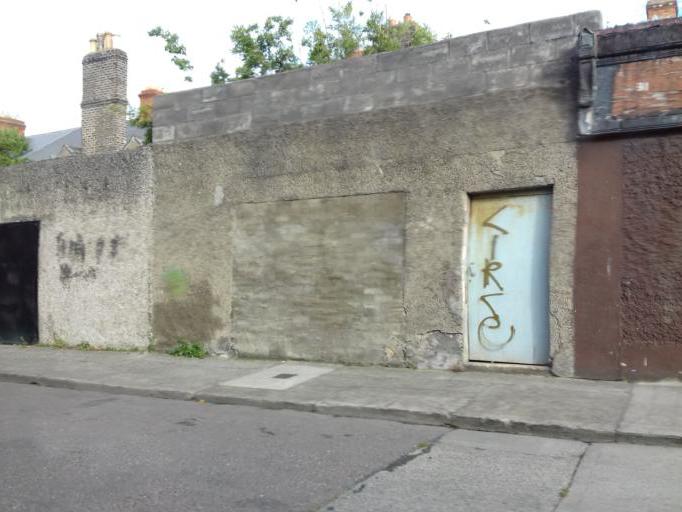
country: IE
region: Leinster
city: Rialto
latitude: 53.3347
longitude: -6.2833
